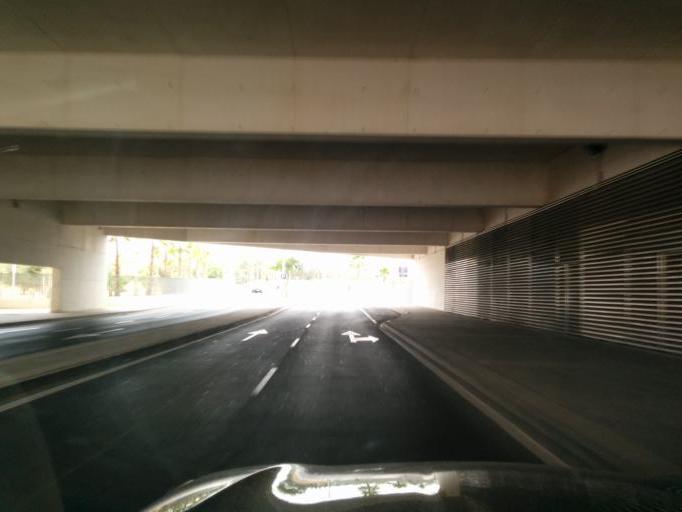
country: ES
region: Andalusia
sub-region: Provincia de Sevilla
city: Sevilla
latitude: 37.4036
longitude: -5.9345
